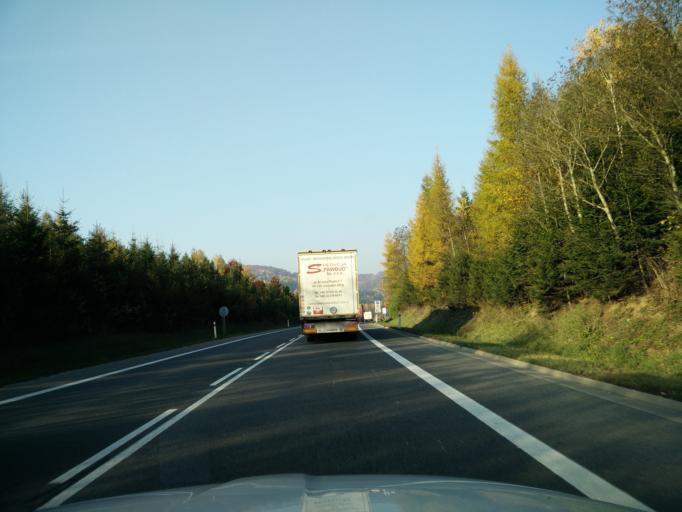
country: SK
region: Zilinsky
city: Cadca
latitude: 49.4167
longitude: 18.8379
